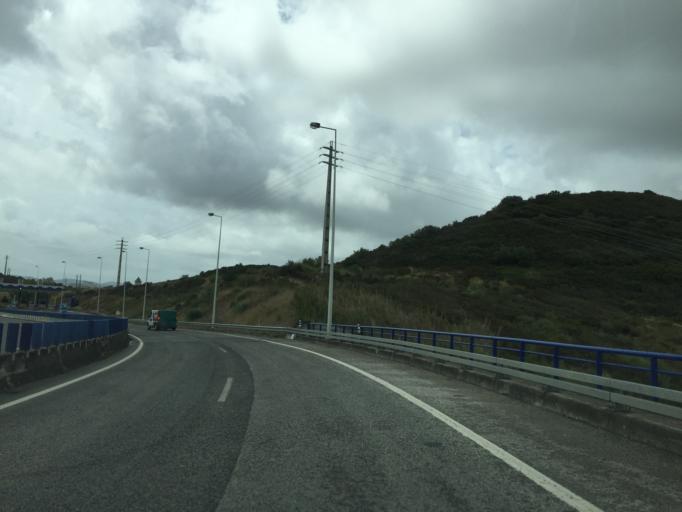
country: PT
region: Lisbon
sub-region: Torres Vedras
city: Torres Vedras
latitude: 39.0635
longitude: -9.2426
